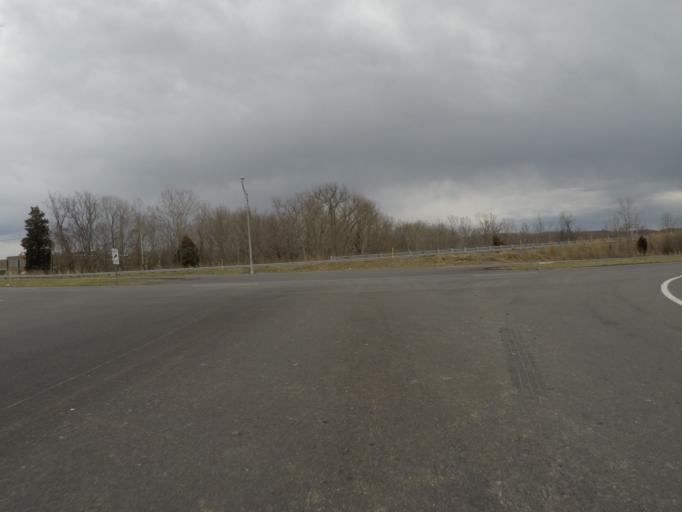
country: US
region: West Virginia
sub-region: Cabell County
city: Huntington
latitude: 38.4239
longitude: -82.4885
